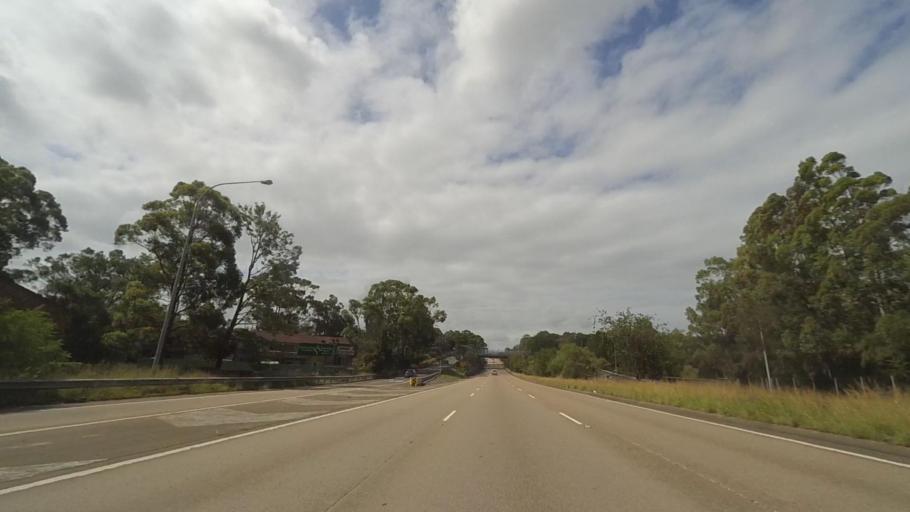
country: AU
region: New South Wales
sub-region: Newcastle
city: North Lambton
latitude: -32.8990
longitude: 151.6943
